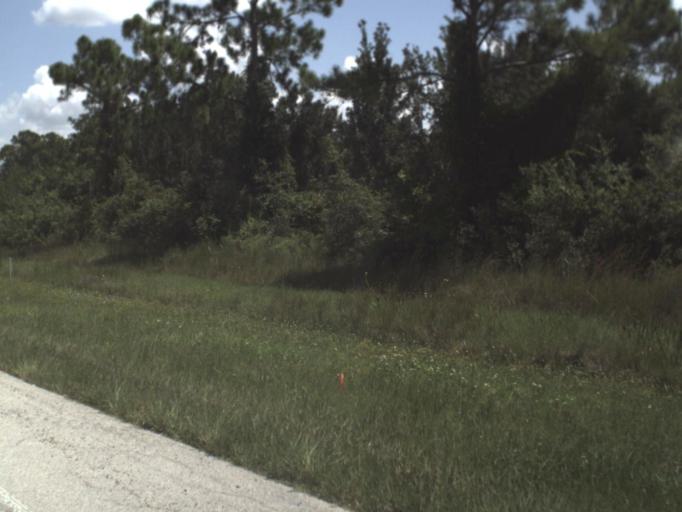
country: US
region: Florida
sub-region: Pinellas County
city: Gandy
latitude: 27.8632
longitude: -82.6444
